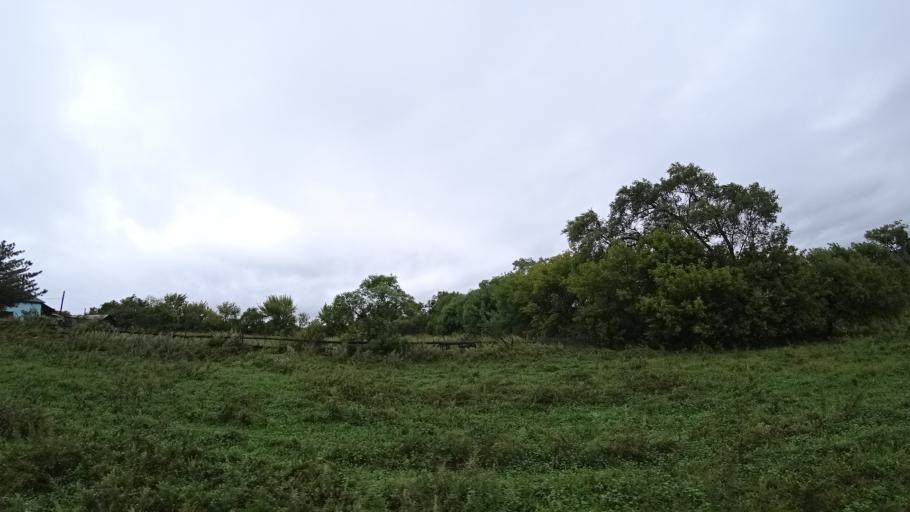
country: RU
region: Primorskiy
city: Monastyrishche
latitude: 44.2642
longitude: 132.4213
